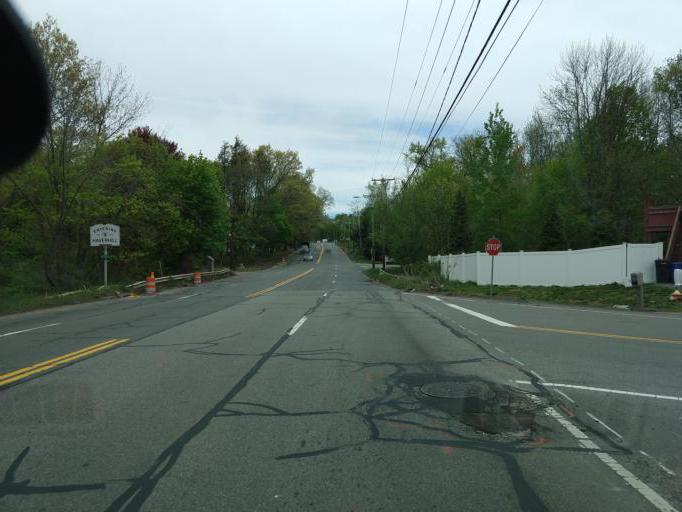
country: US
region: Massachusetts
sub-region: Essex County
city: North Andover
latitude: 42.7381
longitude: -71.1123
